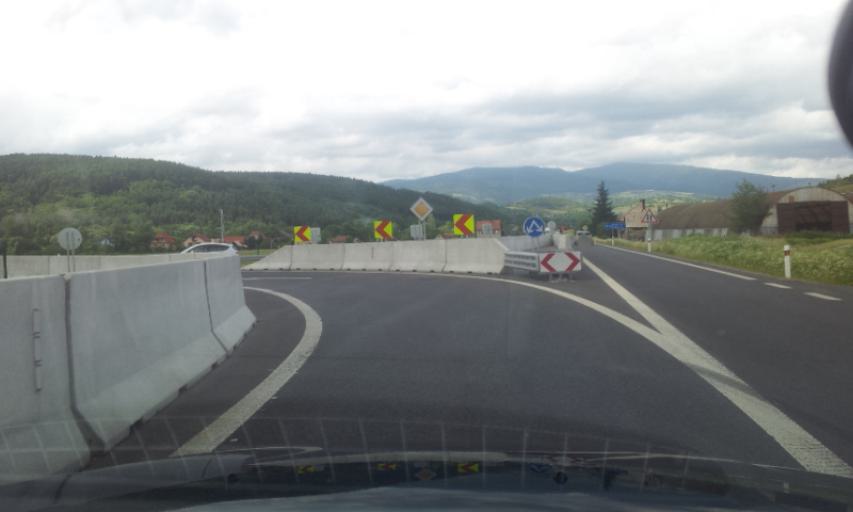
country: SK
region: Banskobystricky
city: Detva
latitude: 48.5338
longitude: 19.4545
